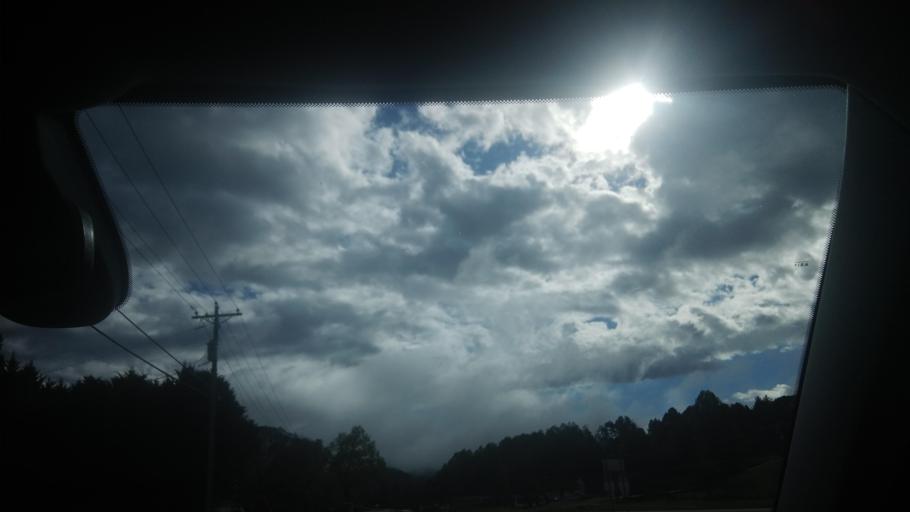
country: US
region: Tennessee
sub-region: Blount County
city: Wildwood
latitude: 35.6788
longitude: -83.7331
